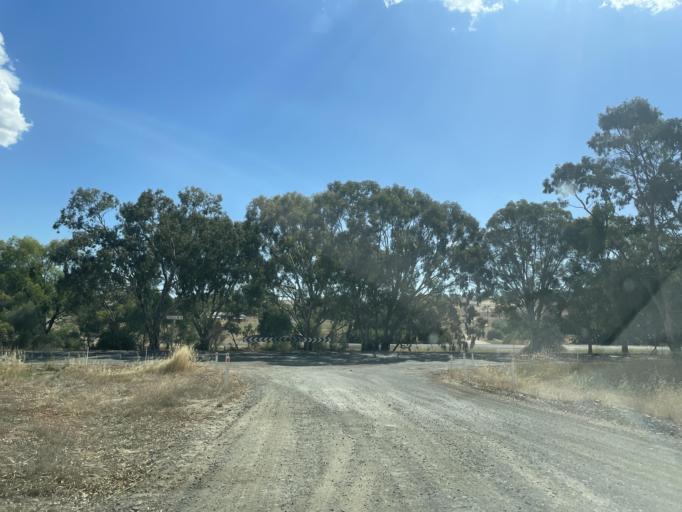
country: AU
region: South Australia
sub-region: Clare and Gilbert Valleys
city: Clare
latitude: -33.9126
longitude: 138.7173
